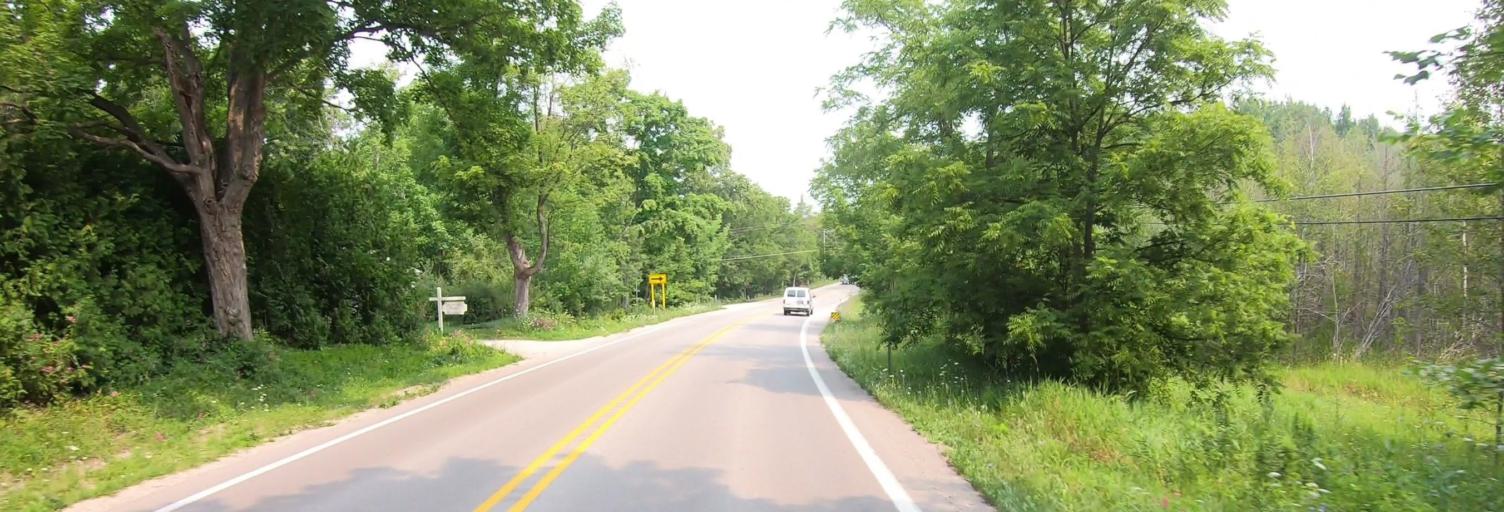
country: US
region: Michigan
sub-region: Leelanau County
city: Leland
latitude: 44.9888
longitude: -85.7722
